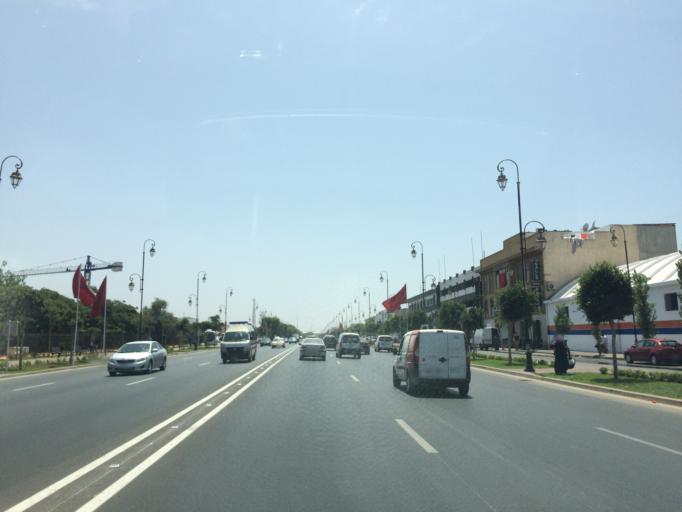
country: MA
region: Rabat-Sale-Zemmour-Zaer
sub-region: Rabat
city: Rabat
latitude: 33.9878
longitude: -6.8686
